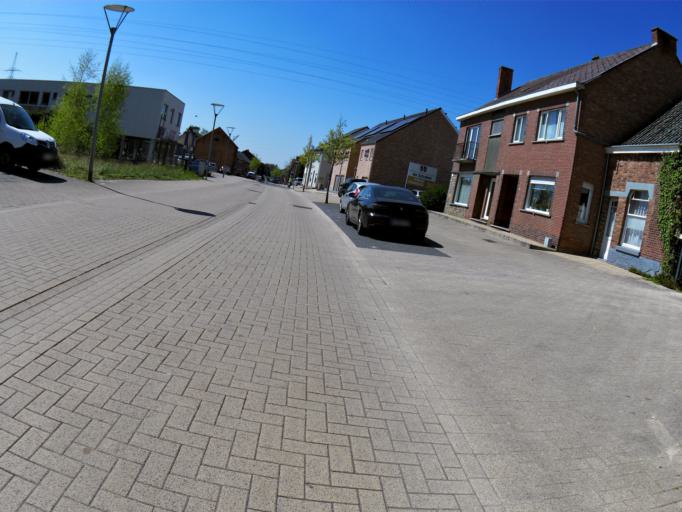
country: BE
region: Flanders
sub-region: Provincie Limburg
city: Houthalen
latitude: 51.0308
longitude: 5.3700
